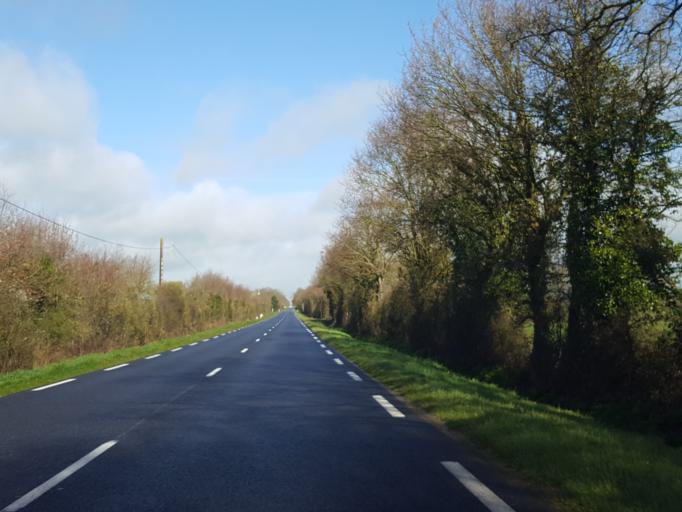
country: FR
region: Pays de la Loire
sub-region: Departement de la Vendee
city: Les Lucs-sur-Boulogne
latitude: 46.8217
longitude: -1.4714
